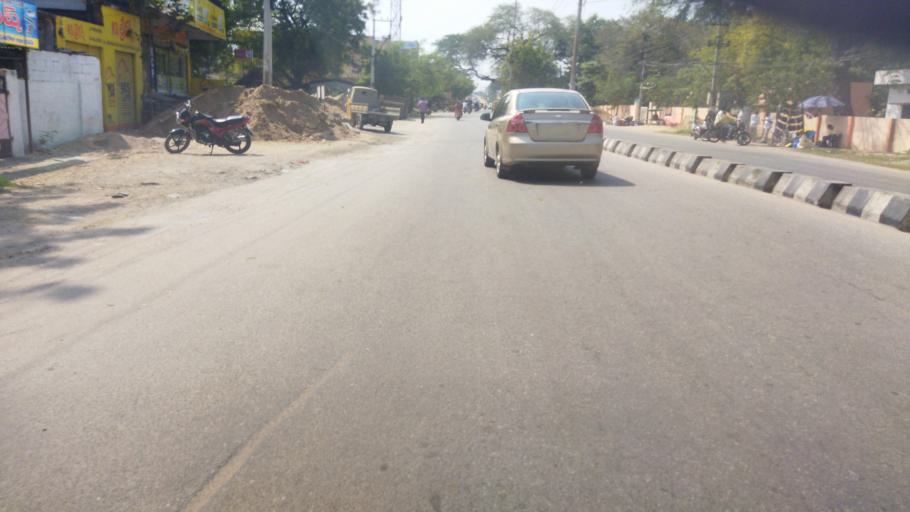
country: IN
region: Telangana
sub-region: Nalgonda
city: Nalgonda
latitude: 17.0702
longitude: 79.2832
